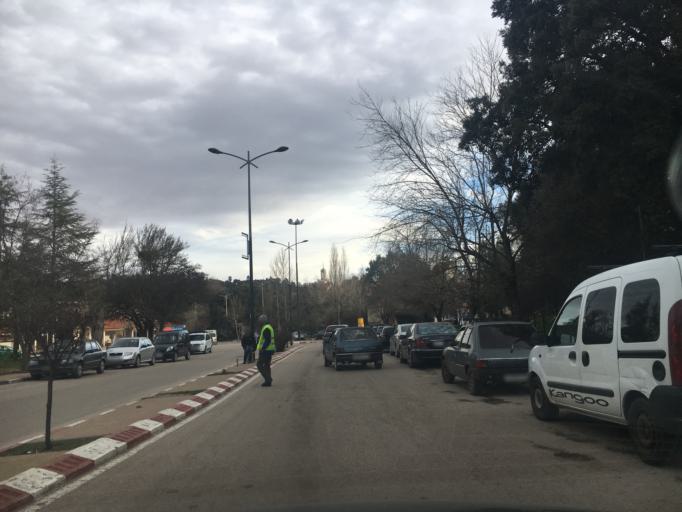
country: MA
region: Meknes-Tafilalet
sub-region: Ifrane
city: Ifrane
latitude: 33.5268
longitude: -5.1171
